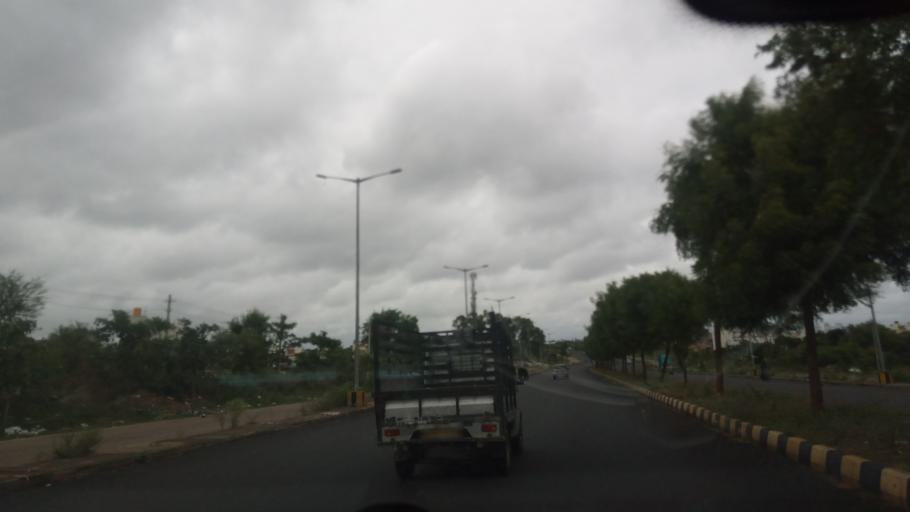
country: IN
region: Karnataka
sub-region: Mysore
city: Mysore
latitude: 12.3165
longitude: 76.5957
